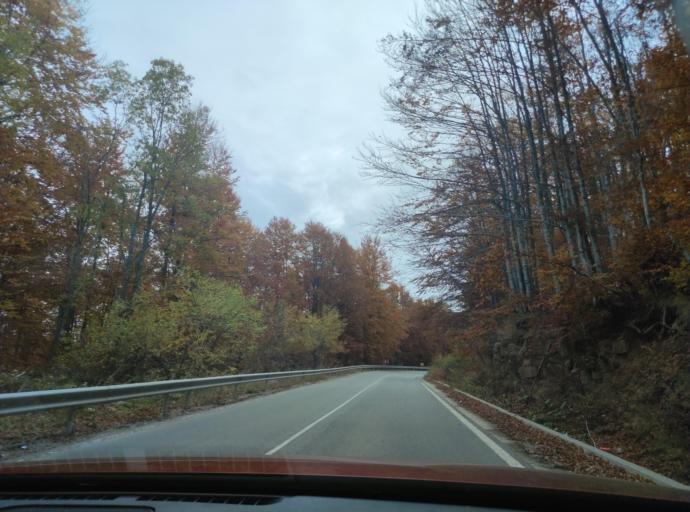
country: BG
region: Sofiya
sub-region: Obshtina Godech
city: Godech
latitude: 43.1075
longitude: 23.1096
